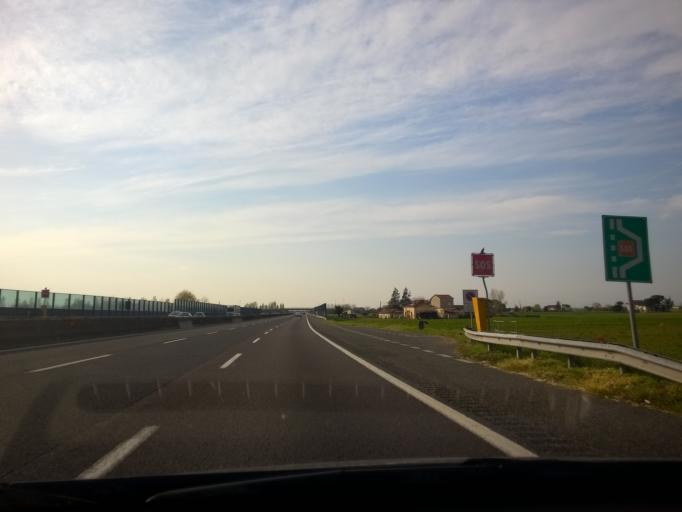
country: IT
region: Emilia-Romagna
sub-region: Forli-Cesena
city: Santa Maria Nuova
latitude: 44.2100
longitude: 12.1889
